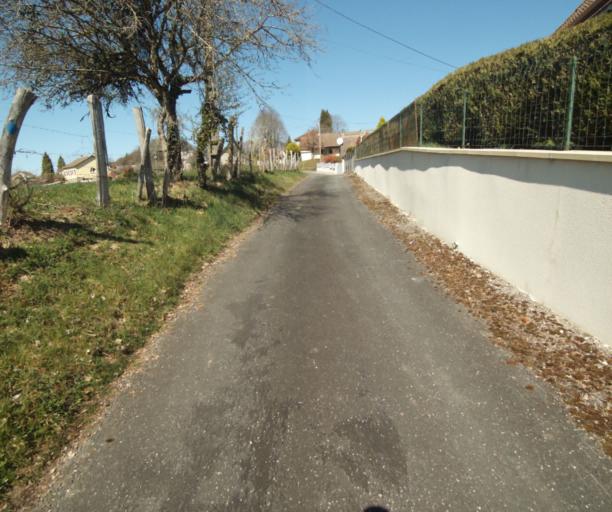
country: FR
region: Limousin
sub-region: Departement de la Correze
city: Saint-Mexant
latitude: 45.2774
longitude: 1.6650
